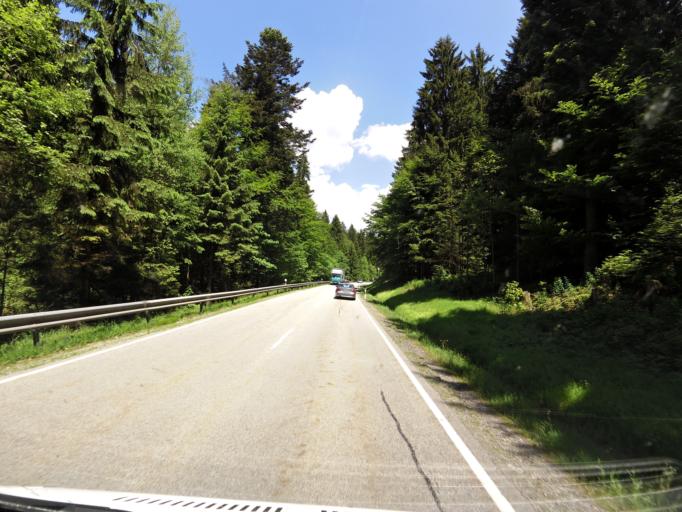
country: DE
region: Bavaria
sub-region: Lower Bavaria
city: Hinterschmiding
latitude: 48.8419
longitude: 13.6124
